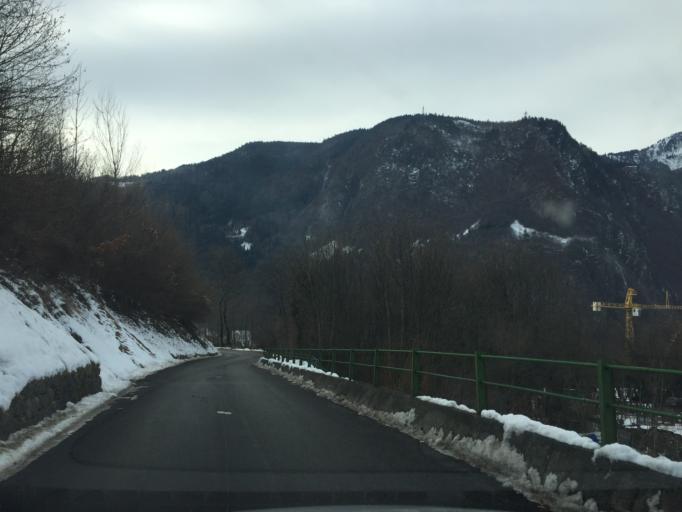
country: FR
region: Rhone-Alpes
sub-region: Departement de la Savoie
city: Aigueblanche
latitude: 45.5228
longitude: 6.4926
